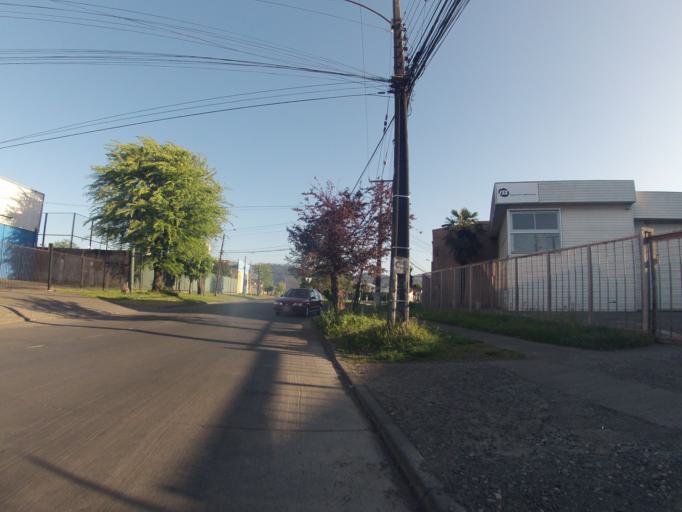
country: CL
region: Araucania
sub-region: Provincia de Cautin
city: Temuco
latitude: -38.7259
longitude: -72.5734
